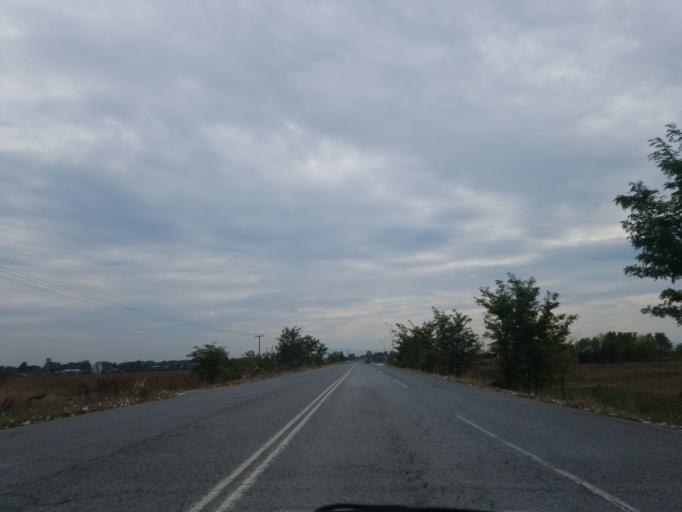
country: GR
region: Thessaly
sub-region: Nomos Kardhitsas
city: Sofades
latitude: 39.3473
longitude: 22.0722
